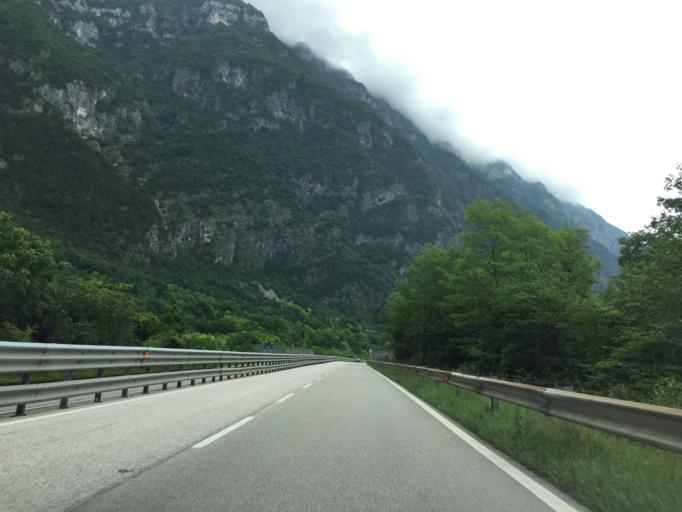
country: IT
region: Trentino-Alto Adige
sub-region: Provincia di Trento
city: Grigno
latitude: 46.0037
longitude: 11.6580
